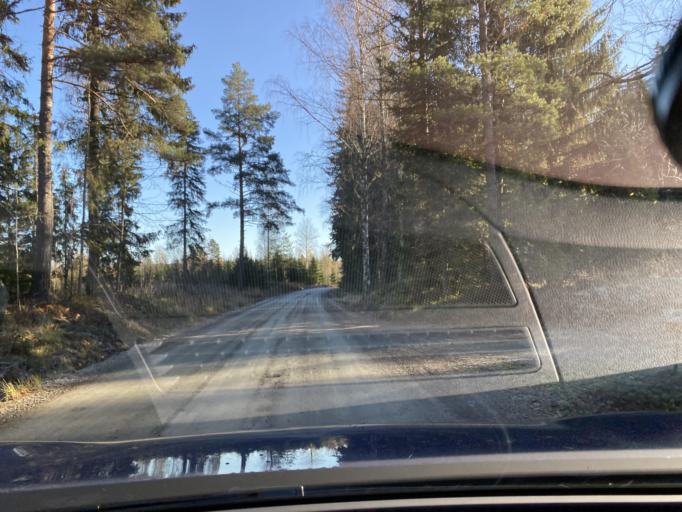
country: FI
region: Haeme
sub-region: Haemeenlinna
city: Kalvola
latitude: 60.9882
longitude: 24.0460
